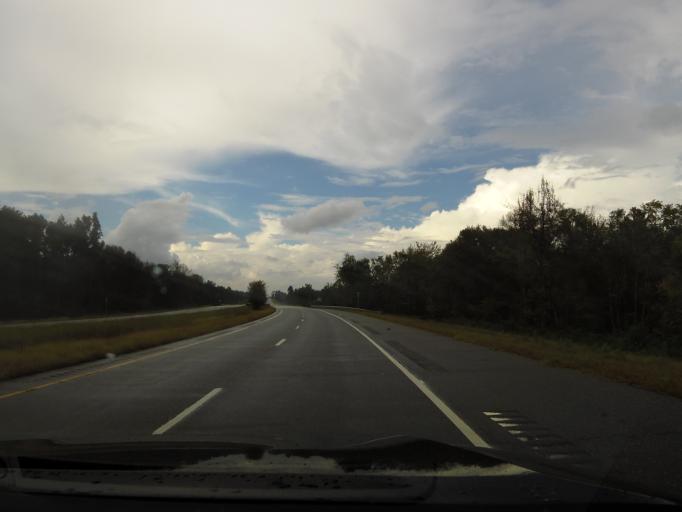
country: US
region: Georgia
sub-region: Wayne County
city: Jesup
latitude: 31.6122
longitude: -81.8599
